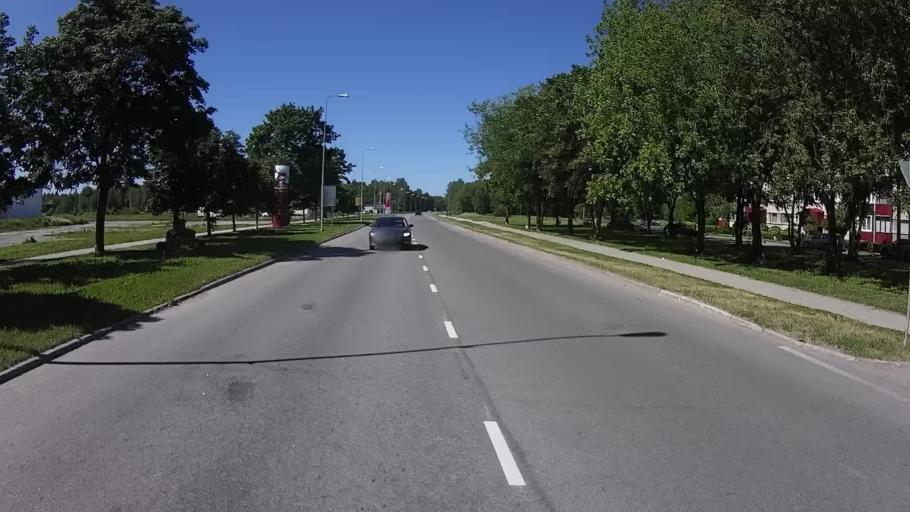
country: EE
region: Ida-Virumaa
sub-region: Kohtla-Jaerve linn
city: Kohtla-Jarve
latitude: 59.4084
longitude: 27.2805
